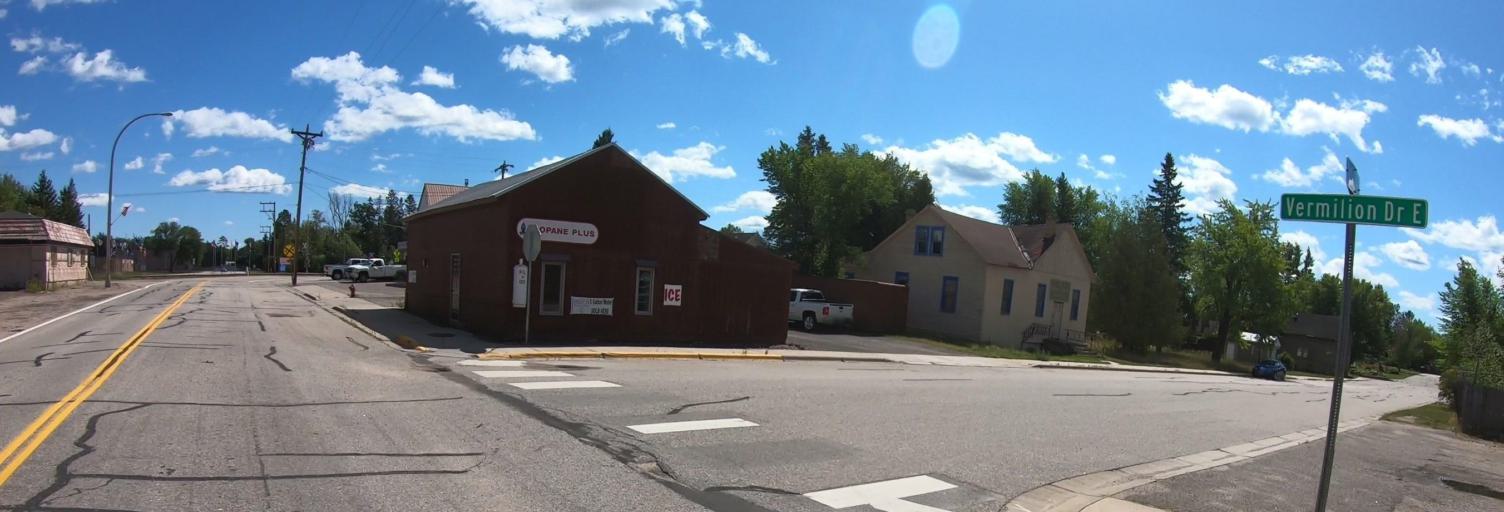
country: US
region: Minnesota
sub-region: Saint Louis County
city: Mountain Iron
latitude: 47.8540
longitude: -92.6876
